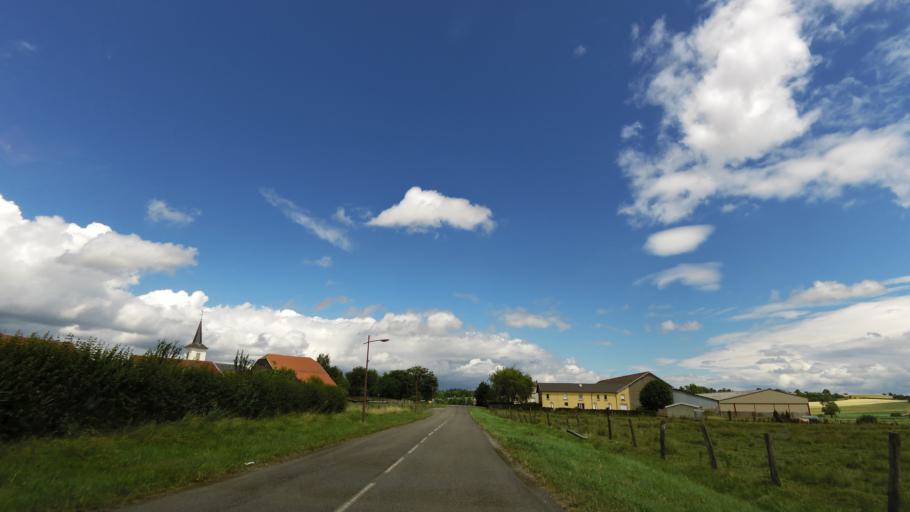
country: FR
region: Lorraine
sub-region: Departement de la Moselle
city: Lorquin
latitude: 48.6297
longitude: 6.9667
